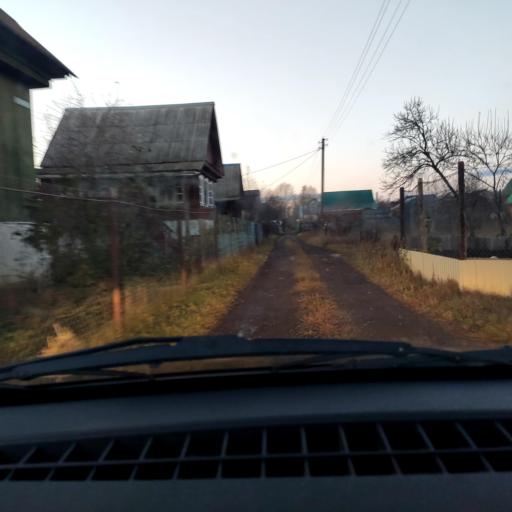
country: RU
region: Bashkortostan
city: Ufa
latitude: 54.6489
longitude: 55.8989
